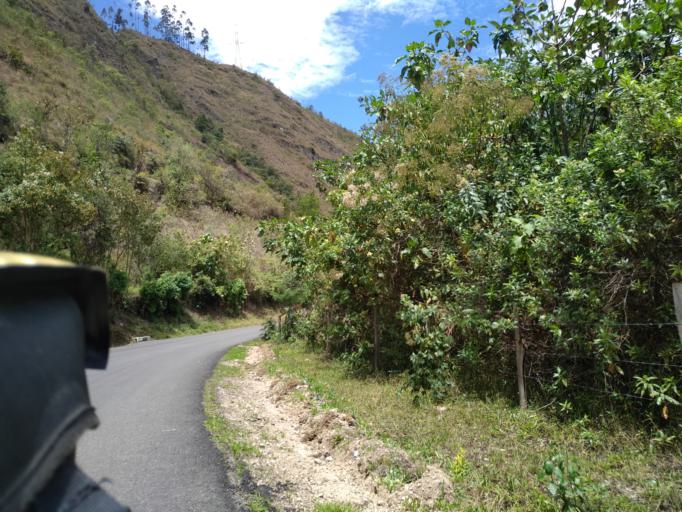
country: PE
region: Amazonas
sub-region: Provincia de Chachapoyas
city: Montevideo
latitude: -6.6626
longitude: -77.7981
